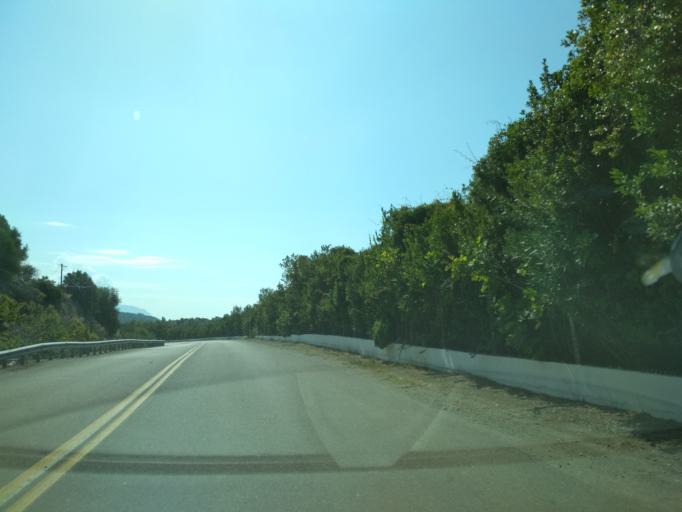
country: GR
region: Central Greece
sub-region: Nomos Evvoias
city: Roviai
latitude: 38.8324
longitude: 23.1997
